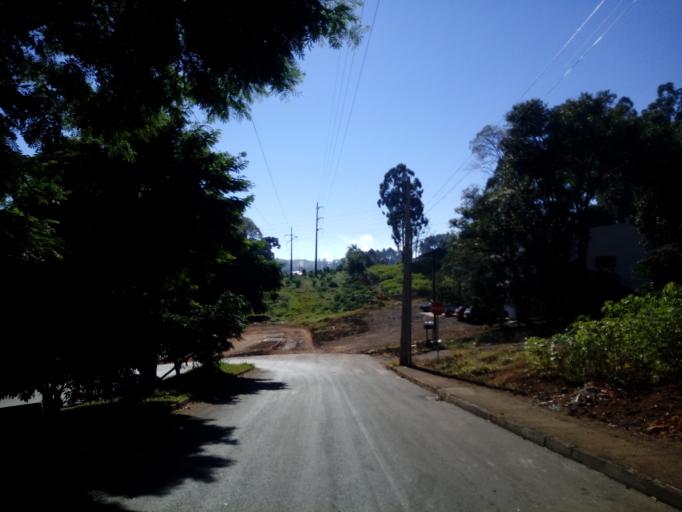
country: BR
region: Santa Catarina
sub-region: Chapeco
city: Chapeco
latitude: -27.0649
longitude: -52.6032
